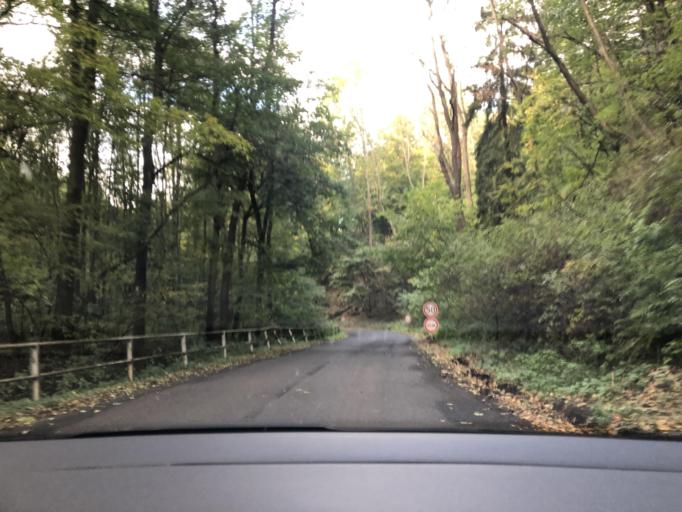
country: CZ
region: Ustecky
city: Velke Brezno
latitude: 50.6334
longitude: 14.1585
